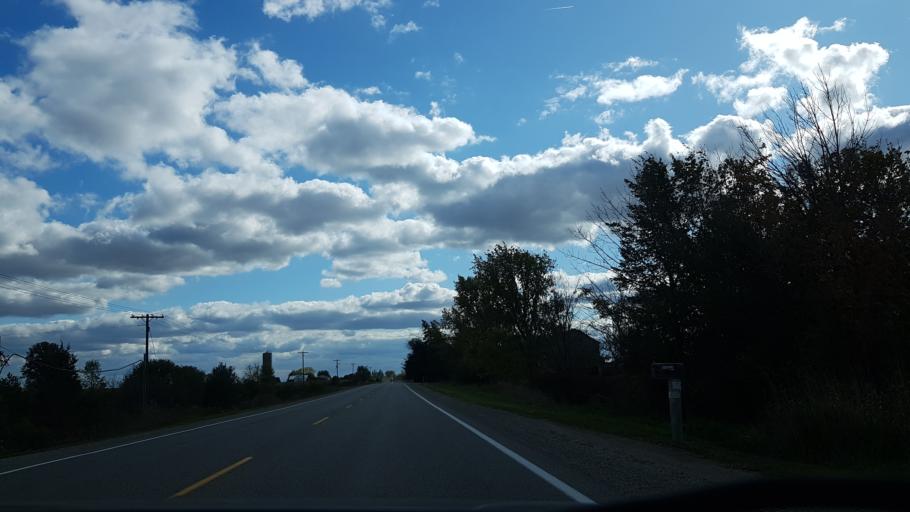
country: CA
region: Ontario
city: South Huron
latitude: 43.2289
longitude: -81.6877
